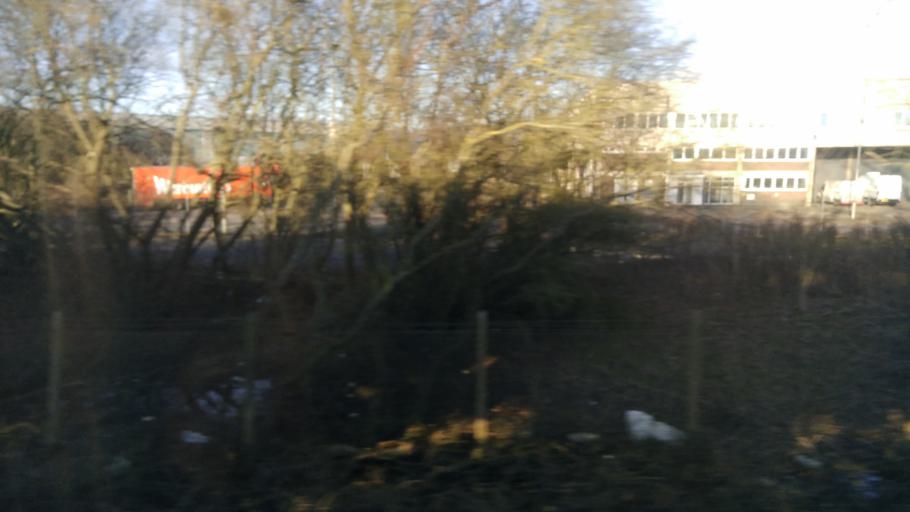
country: GB
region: England
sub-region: Kent
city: Paddock Wood
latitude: 51.1820
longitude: 0.3965
